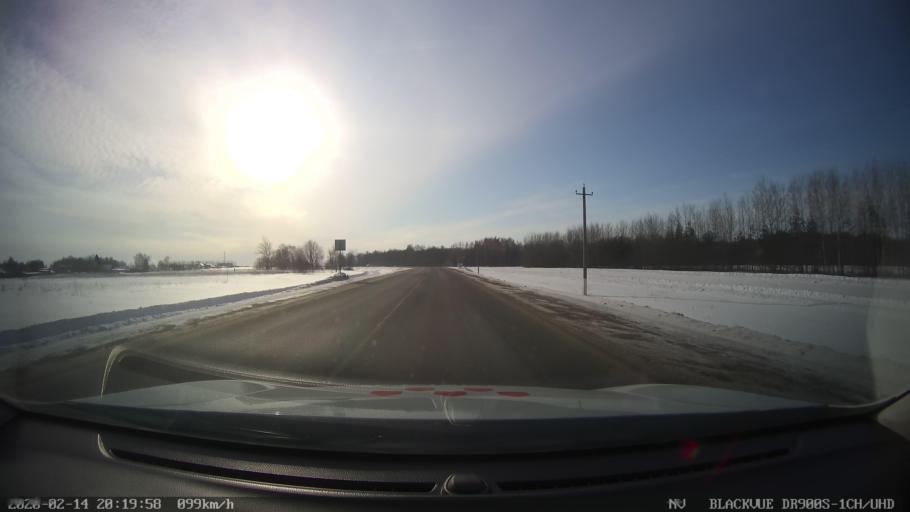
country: RU
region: Tatarstan
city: Verkhniy Uslon
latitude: 55.5626
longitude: 48.9017
